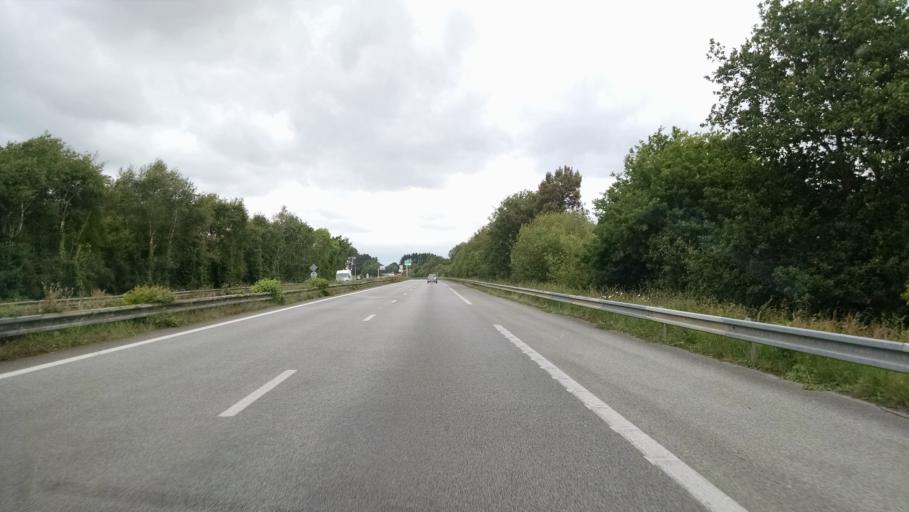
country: FR
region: Brittany
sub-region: Departement du Finistere
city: Redene
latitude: 47.8433
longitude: -3.4995
